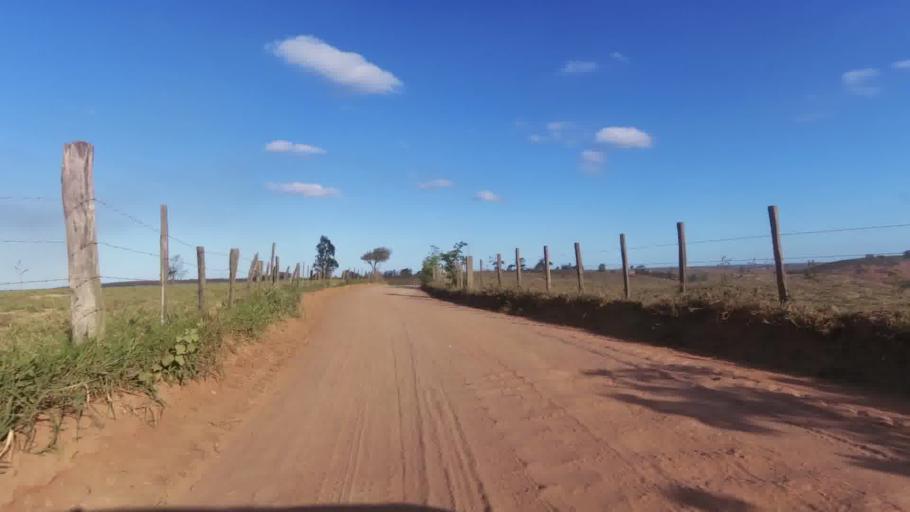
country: BR
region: Espirito Santo
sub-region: Marataizes
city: Marataizes
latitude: -21.1557
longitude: -41.0608
